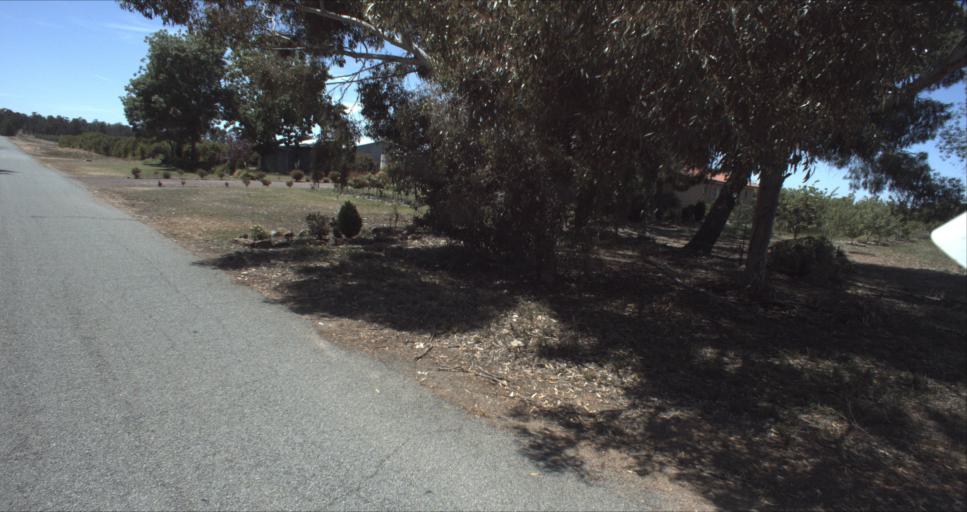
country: AU
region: New South Wales
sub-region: Narrandera
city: Narrandera
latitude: -34.6769
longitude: 146.4412
